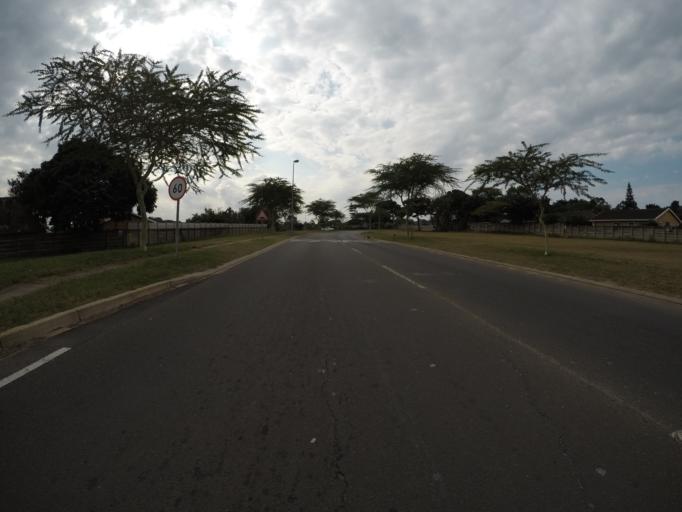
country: ZA
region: KwaZulu-Natal
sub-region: uThungulu District Municipality
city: Richards Bay
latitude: -28.7397
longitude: 32.0776
